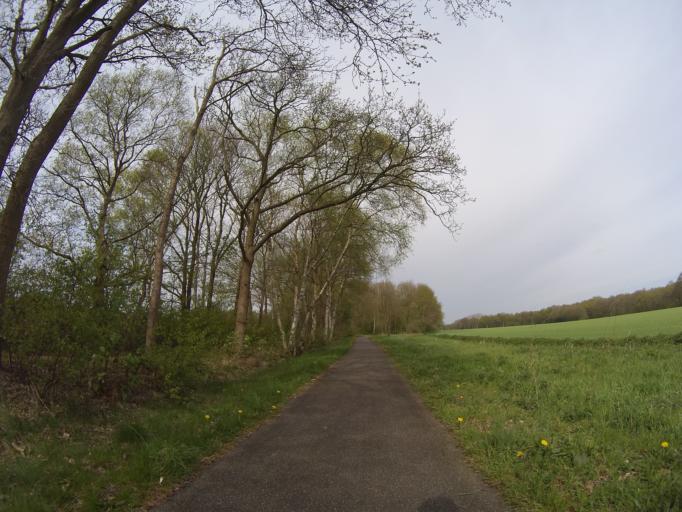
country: NL
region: Drenthe
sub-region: Gemeente Coevorden
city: Sleen
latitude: 52.8355
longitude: 6.6760
